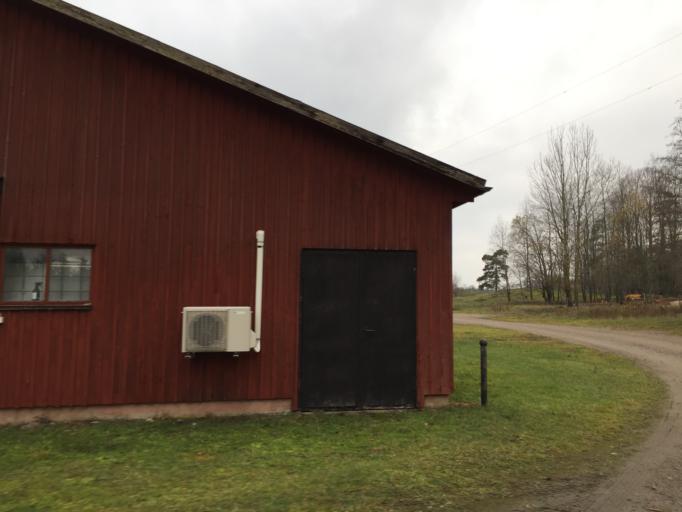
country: SE
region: OErebro
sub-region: Orebro Kommun
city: Odensbacken
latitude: 59.0153
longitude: 15.5894
